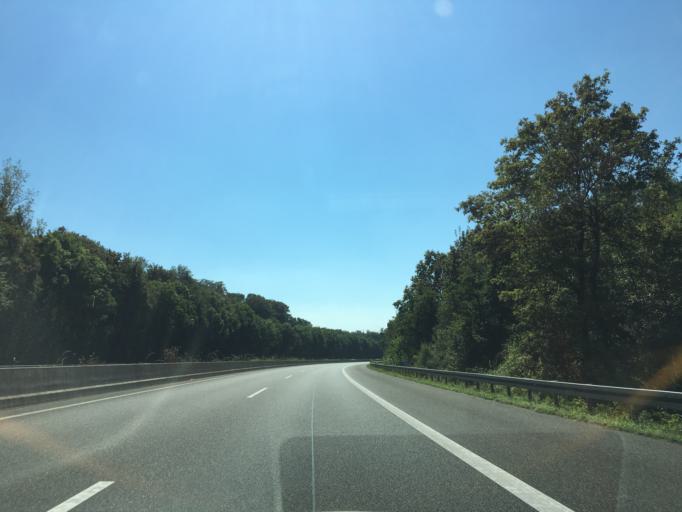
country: DE
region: Hesse
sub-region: Regierungsbezirk Darmstadt
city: Egelsbach
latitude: 49.9785
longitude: 8.6964
